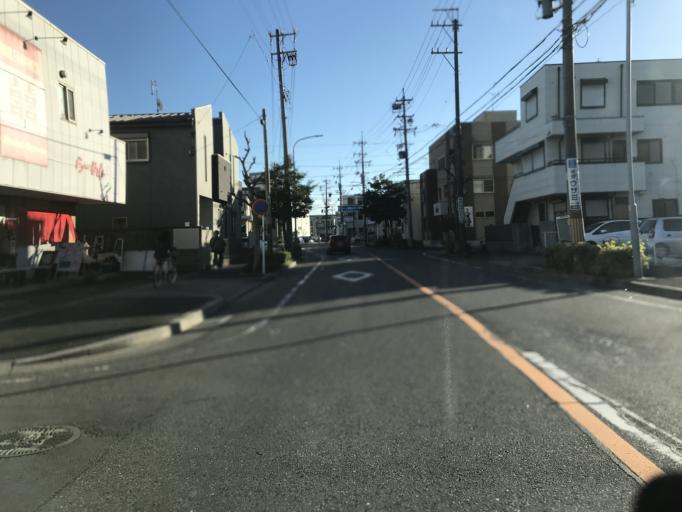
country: JP
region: Aichi
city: Nagoya-shi
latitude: 35.1262
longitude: 136.8797
